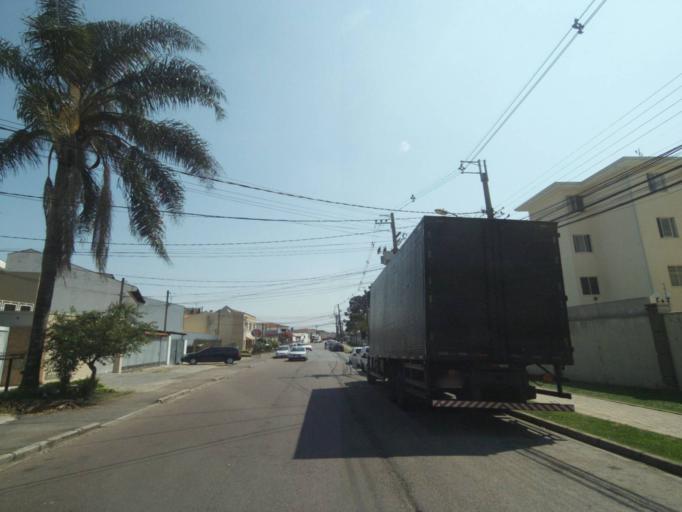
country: BR
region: Parana
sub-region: Curitiba
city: Curitiba
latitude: -25.4791
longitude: -49.3220
